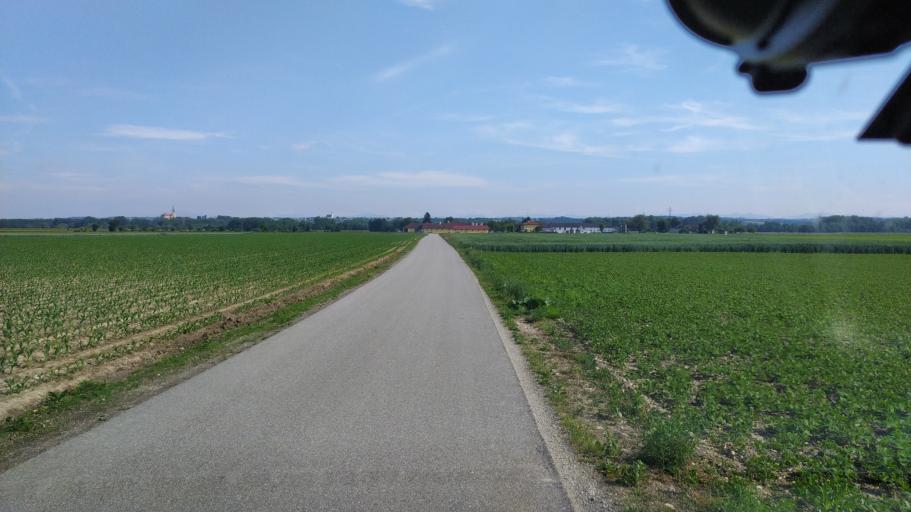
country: AT
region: Lower Austria
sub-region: Politischer Bezirk Amstetten
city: Strengberg
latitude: 48.1878
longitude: 14.6855
